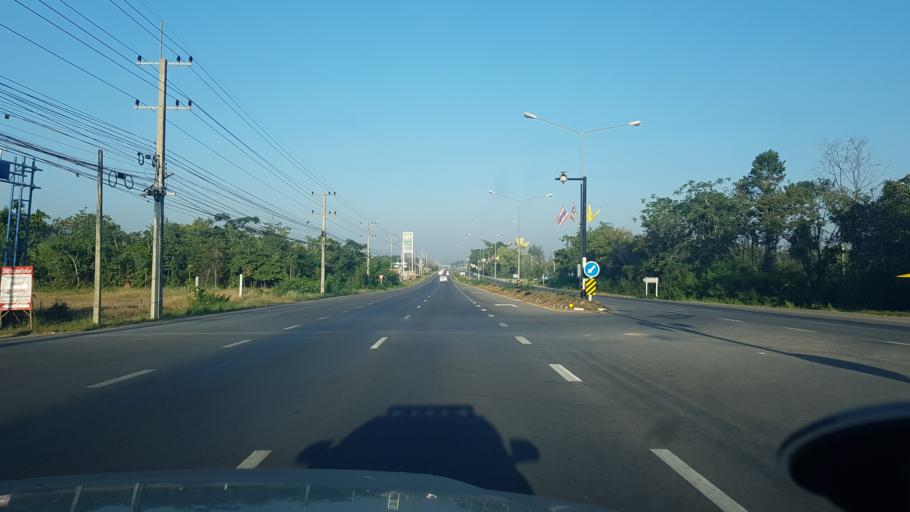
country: TH
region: Khon Kaen
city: Chum Phae
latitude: 16.5769
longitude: 102.0271
